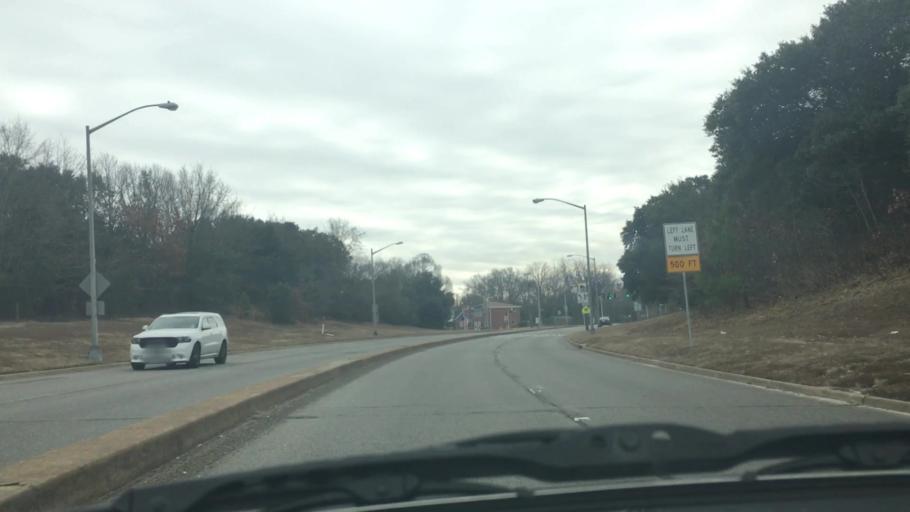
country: US
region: Virginia
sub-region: City of Hampton
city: East Hampton
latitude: 36.9574
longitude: -76.2585
